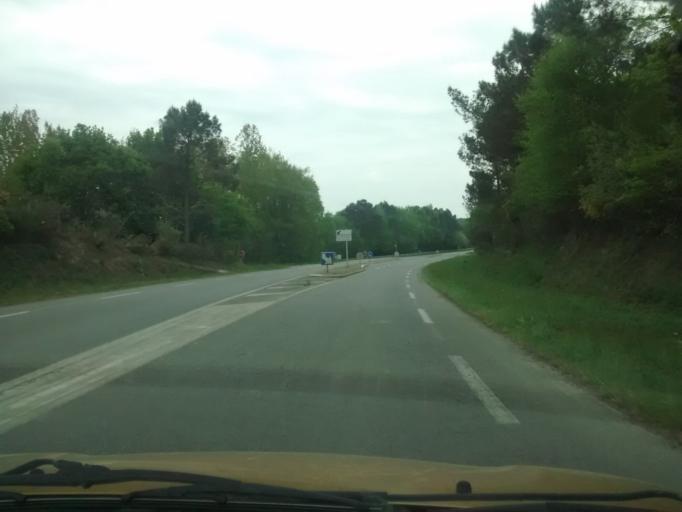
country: FR
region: Brittany
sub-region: Departement du Morbihan
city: Berric
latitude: 47.6008
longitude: -2.5487
